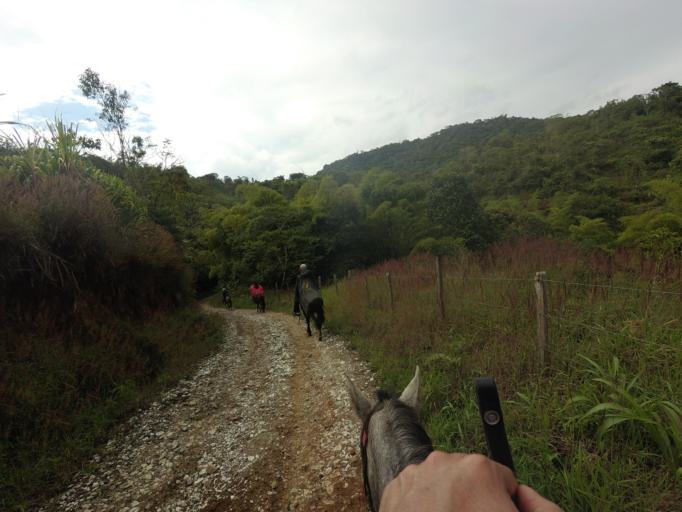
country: CO
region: Huila
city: San Agustin
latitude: 1.9081
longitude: -76.2940
